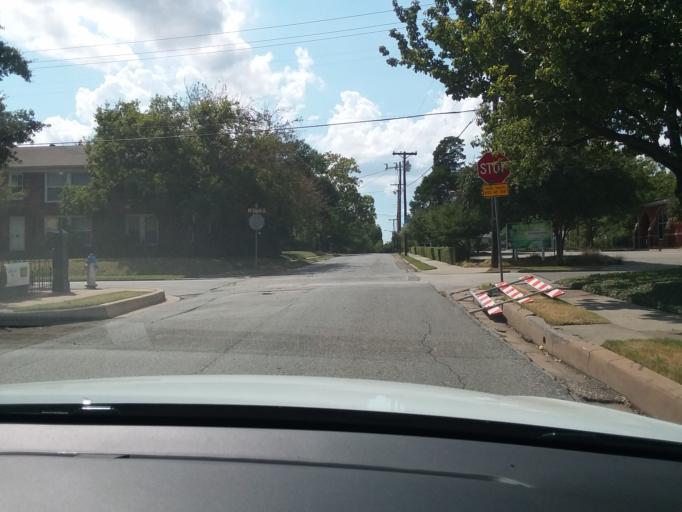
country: US
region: Texas
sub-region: Collin County
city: McKinney
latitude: 33.1993
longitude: -96.6171
